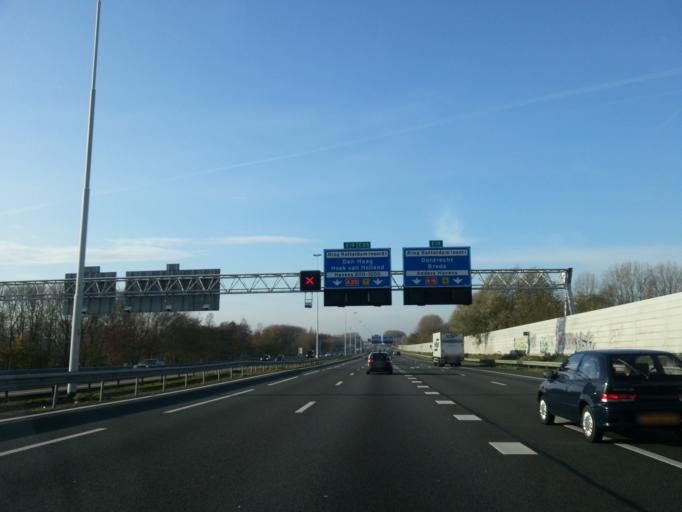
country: NL
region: South Holland
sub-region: Gemeente Rotterdam
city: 's-Gravenland
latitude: 51.9535
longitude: 4.5483
